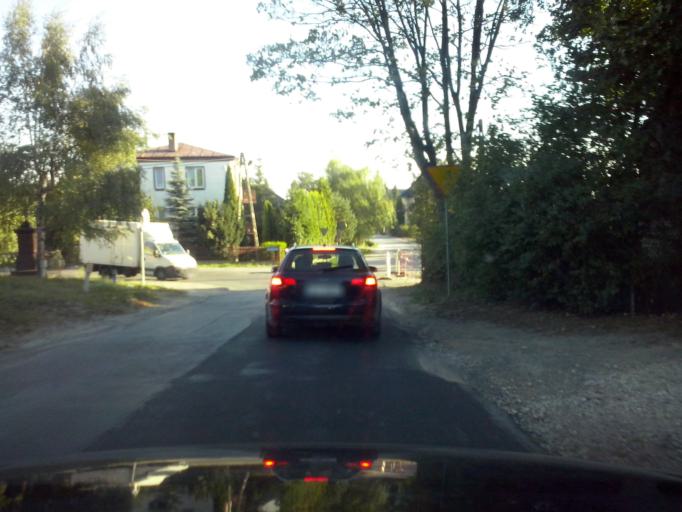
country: PL
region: Swietokrzyskie
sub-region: Powiat kielecki
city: Kielce
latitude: 50.8196
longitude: 20.6256
